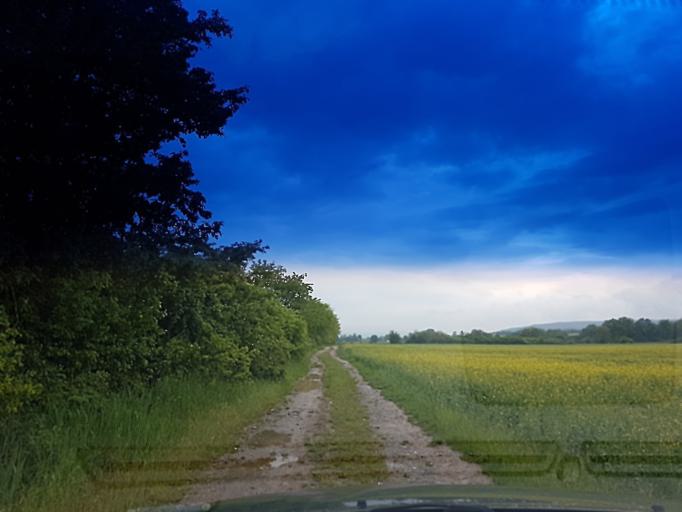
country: DE
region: Bavaria
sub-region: Upper Franconia
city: Zapfendorf
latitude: 50.0259
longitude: 10.9142
